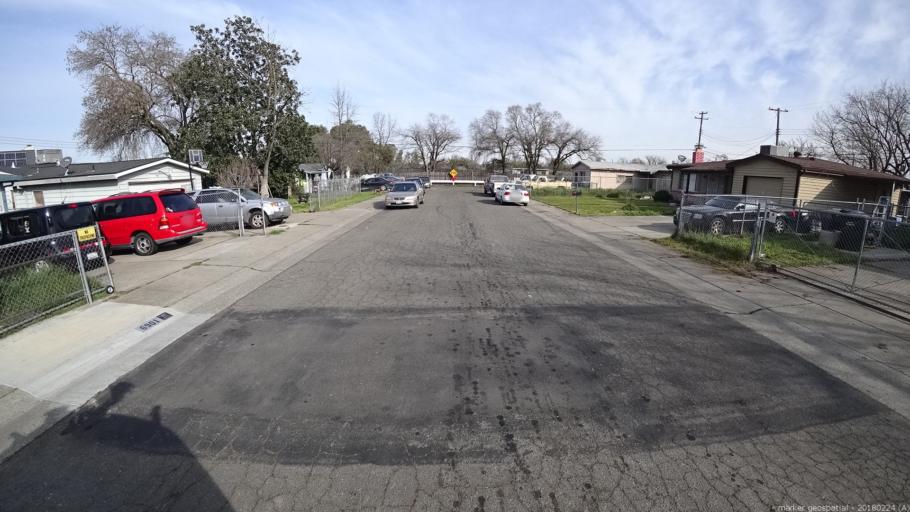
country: US
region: California
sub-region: Sacramento County
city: Rio Linda
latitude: 38.6935
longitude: -121.4588
